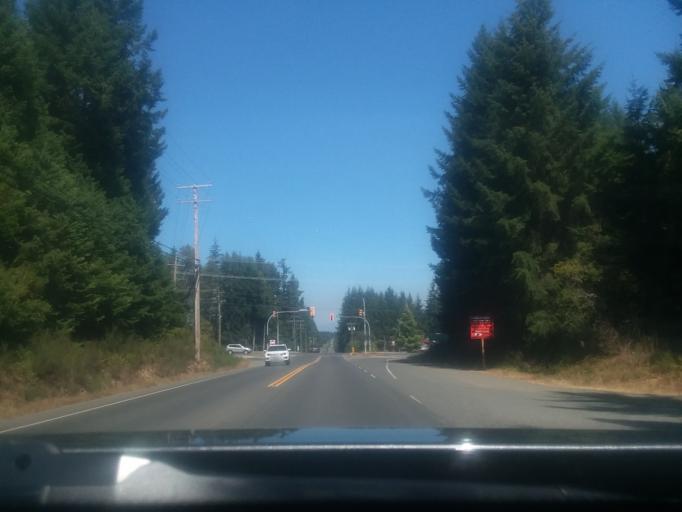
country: CA
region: British Columbia
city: Courtenay
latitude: 49.7141
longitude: -124.9337
